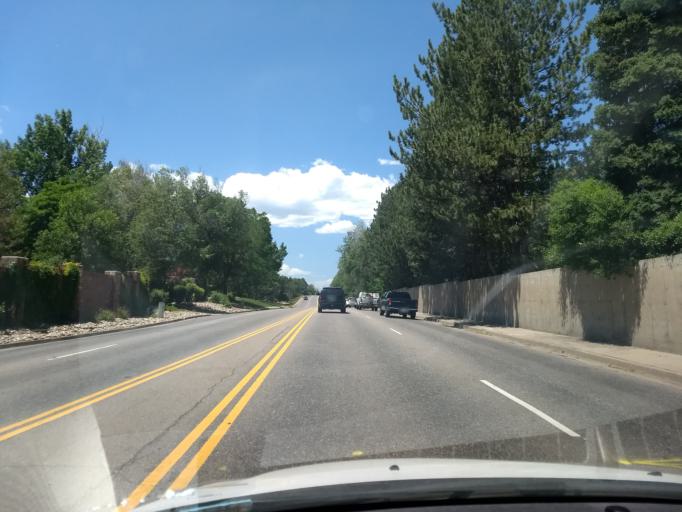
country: US
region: Colorado
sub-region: Arapahoe County
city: Greenwood Village
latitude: 39.6242
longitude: -104.9651
